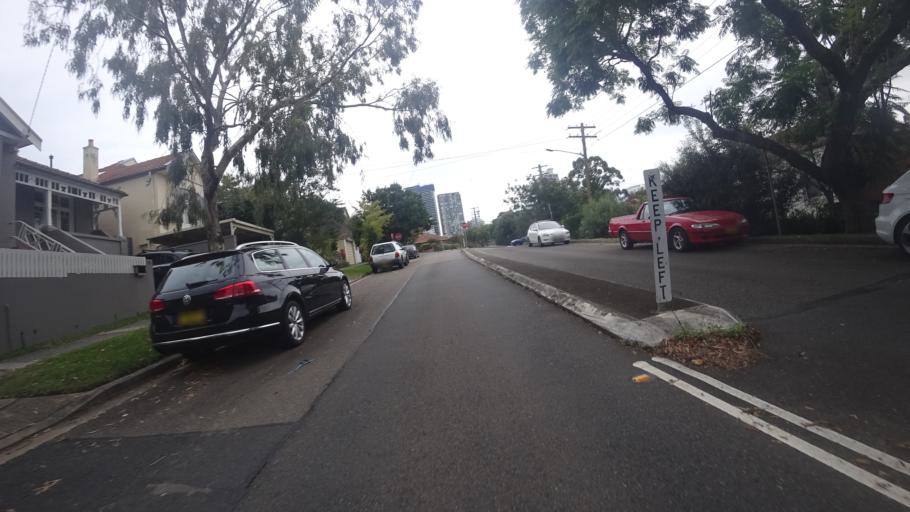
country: AU
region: New South Wales
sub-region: North Sydney
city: St Leonards
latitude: -33.8179
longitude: 151.1980
